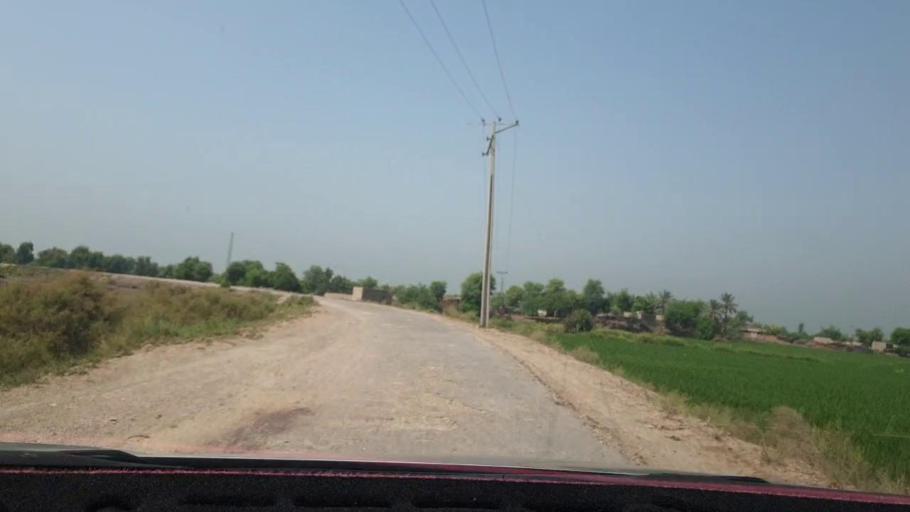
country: PK
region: Sindh
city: Warah
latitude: 27.4176
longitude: 67.8453
